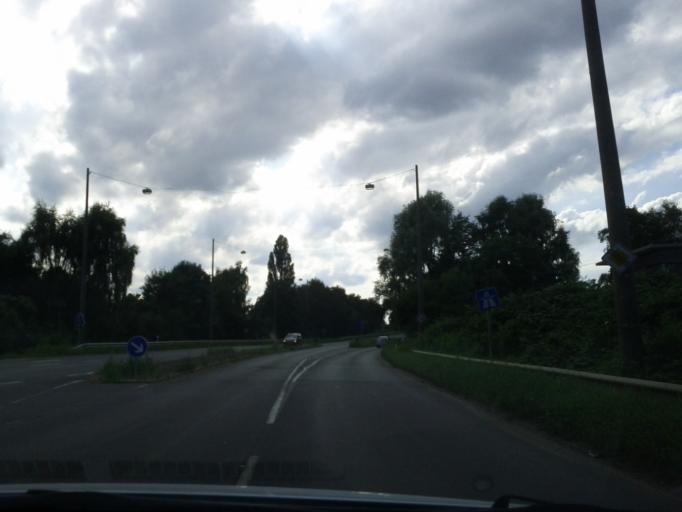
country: DE
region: Bremen
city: Bremen
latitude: 53.1114
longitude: 8.8154
